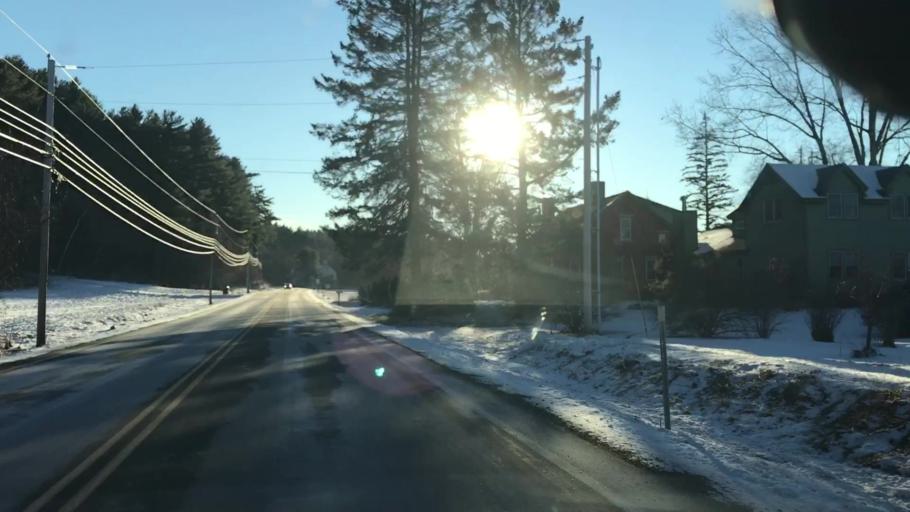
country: US
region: New Hampshire
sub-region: Grafton County
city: Orford
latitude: 43.9159
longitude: -72.1190
